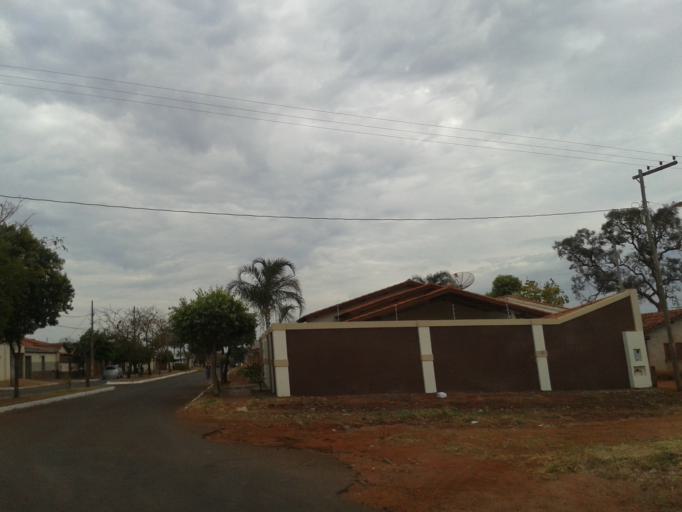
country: BR
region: Minas Gerais
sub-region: Santa Vitoria
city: Santa Vitoria
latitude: -18.8563
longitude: -50.1219
